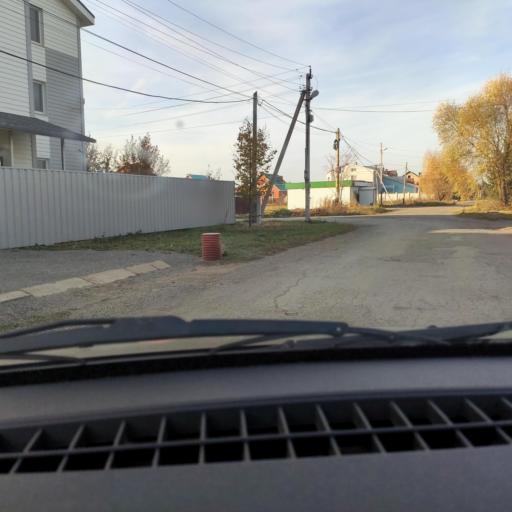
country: RU
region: Bashkortostan
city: Ufa
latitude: 54.6492
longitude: 55.9261
